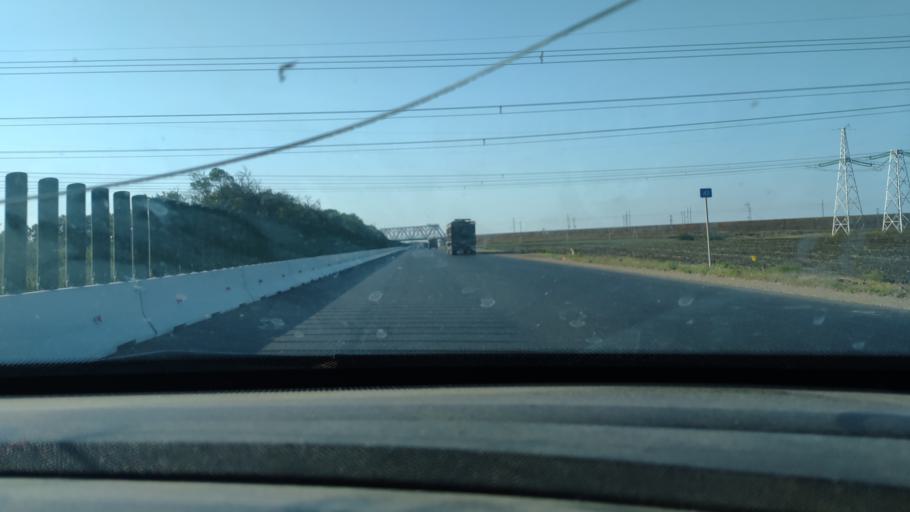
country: RU
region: Krasnodarskiy
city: Medvedovskaya
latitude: 45.4887
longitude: 38.9594
